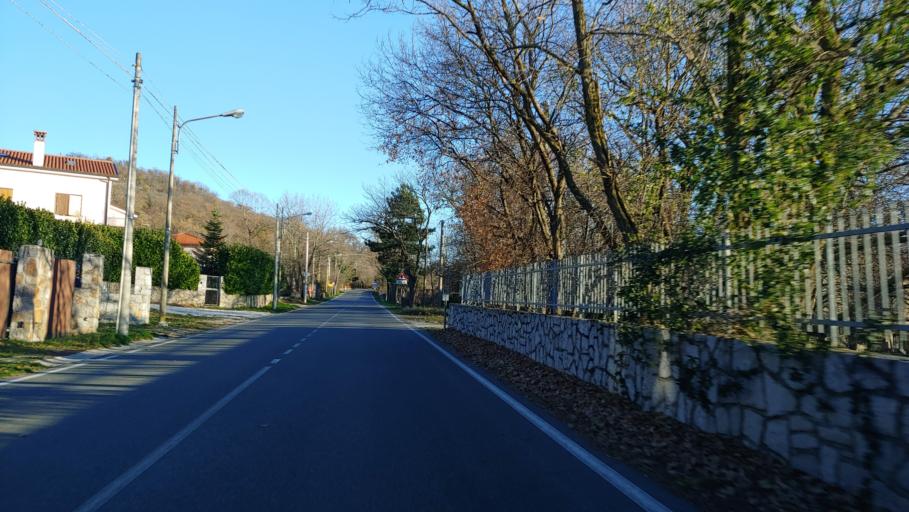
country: IT
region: Friuli Venezia Giulia
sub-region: Provincia di Trieste
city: Zolla
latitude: 45.7101
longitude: 13.8056
